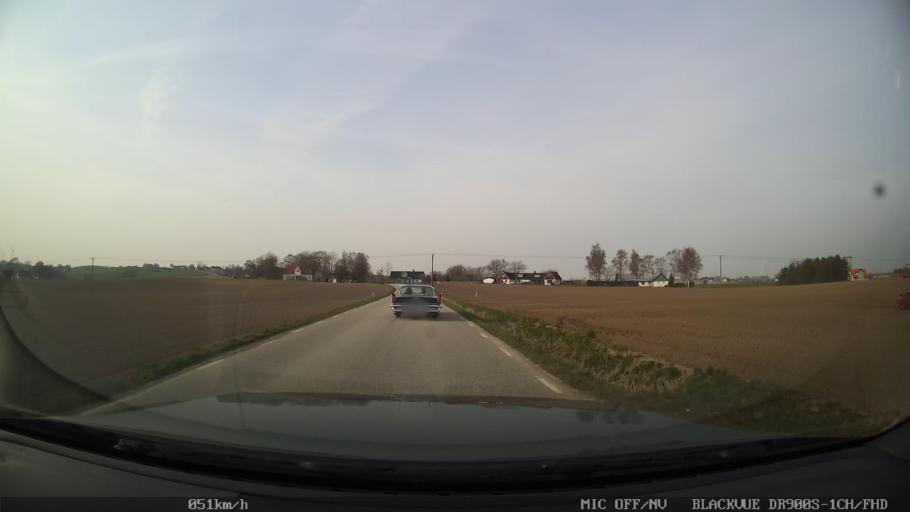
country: SE
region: Skane
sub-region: Ystads Kommun
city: Ystad
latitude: 55.4617
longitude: 13.8248
